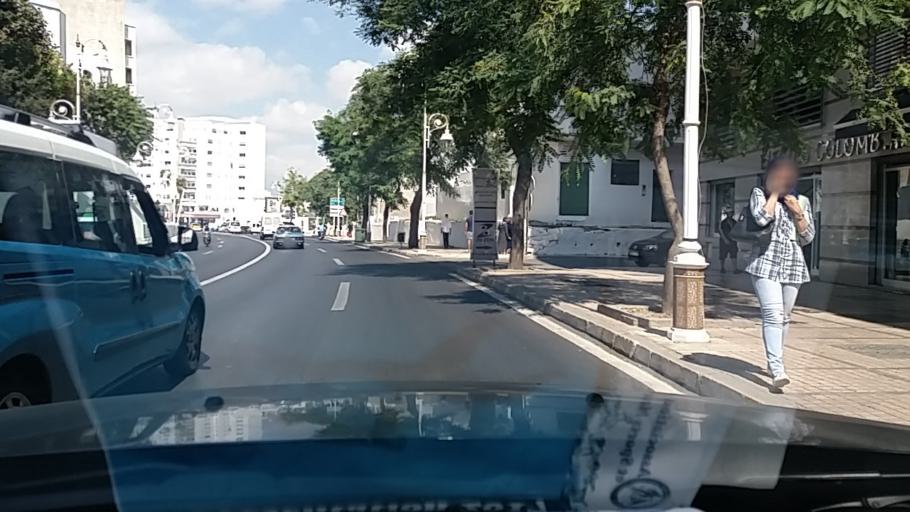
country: MA
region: Tanger-Tetouan
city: Tetouan
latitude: 35.5700
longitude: -5.3597
